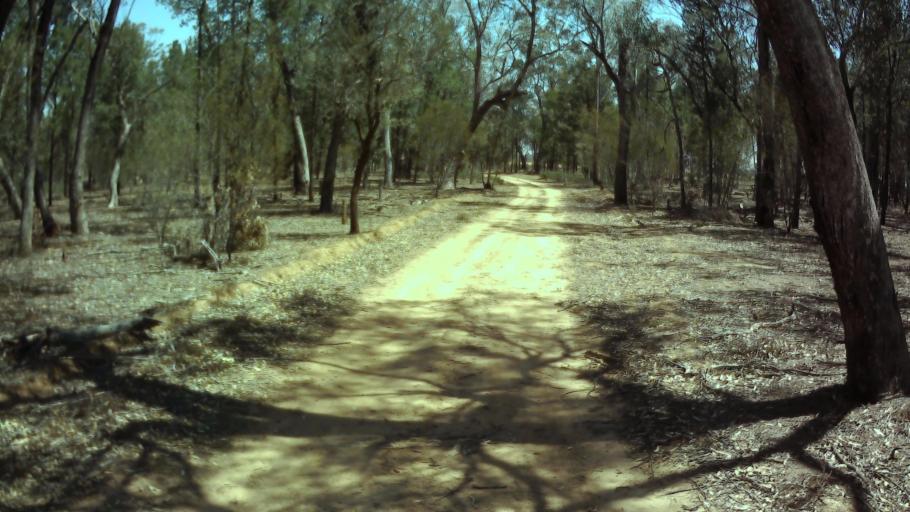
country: AU
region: New South Wales
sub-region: Weddin
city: Grenfell
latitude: -34.0728
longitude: 147.7858
